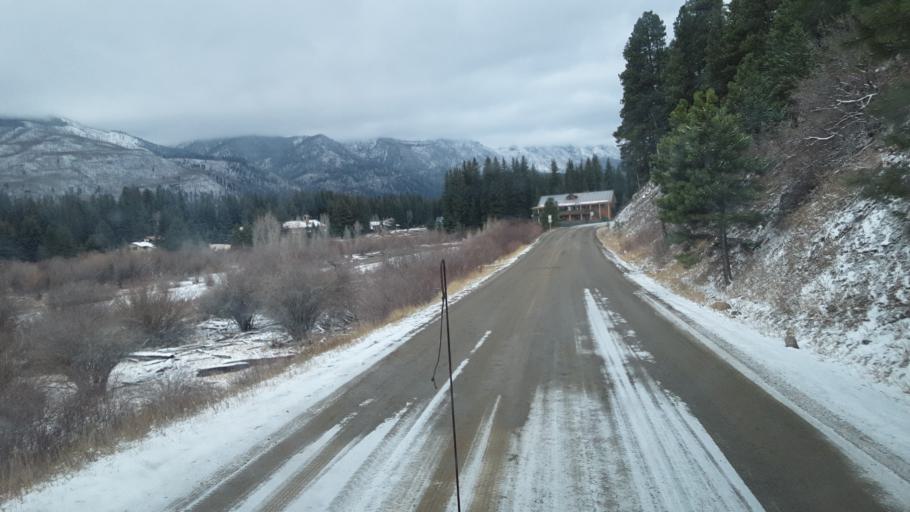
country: US
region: Colorado
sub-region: La Plata County
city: Bayfield
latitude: 37.4333
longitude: -107.5429
